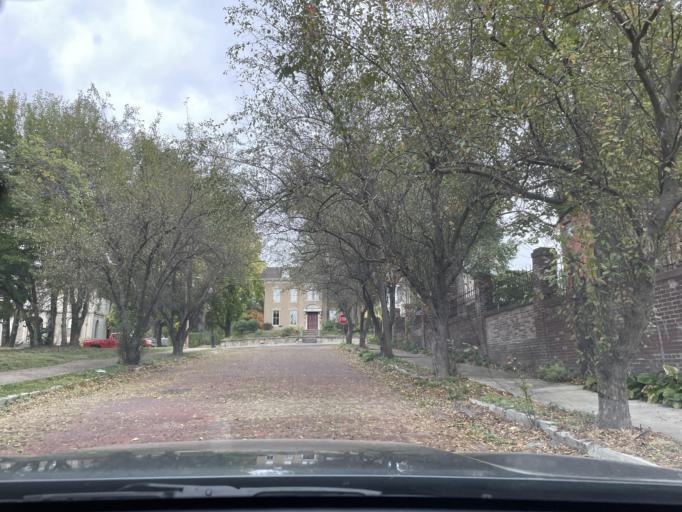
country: US
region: Missouri
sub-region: Buchanan County
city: Saint Joseph
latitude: 39.7719
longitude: -94.8508
